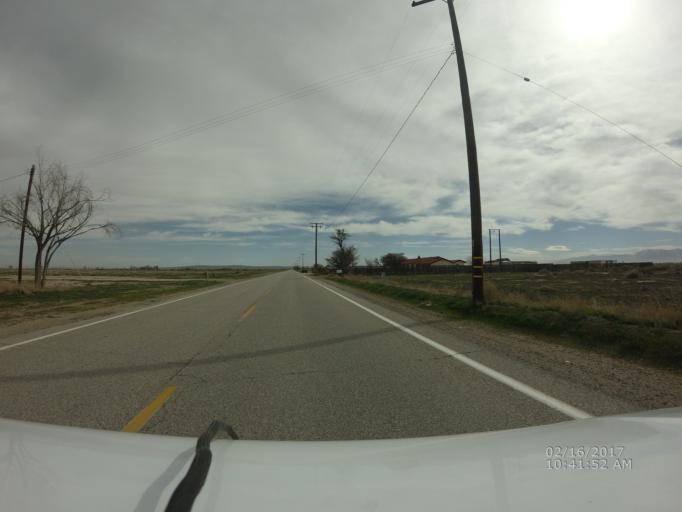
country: US
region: California
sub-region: Los Angeles County
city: Lancaster
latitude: 34.7196
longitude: -117.9834
